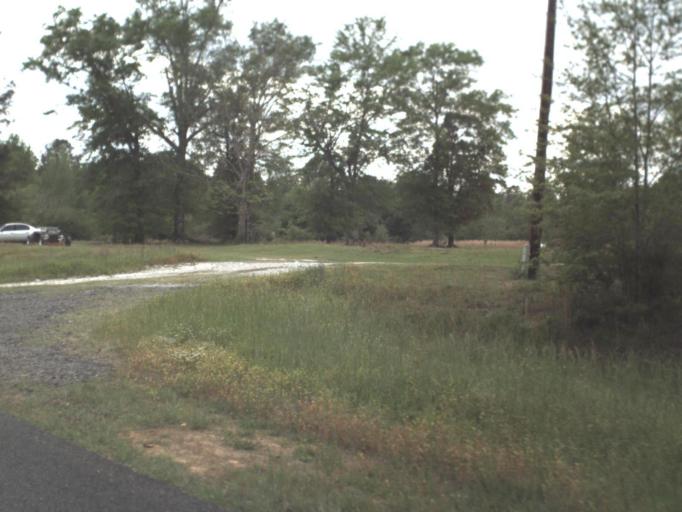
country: US
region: Florida
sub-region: Escambia County
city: Molino
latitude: 30.8256
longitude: -87.3337
